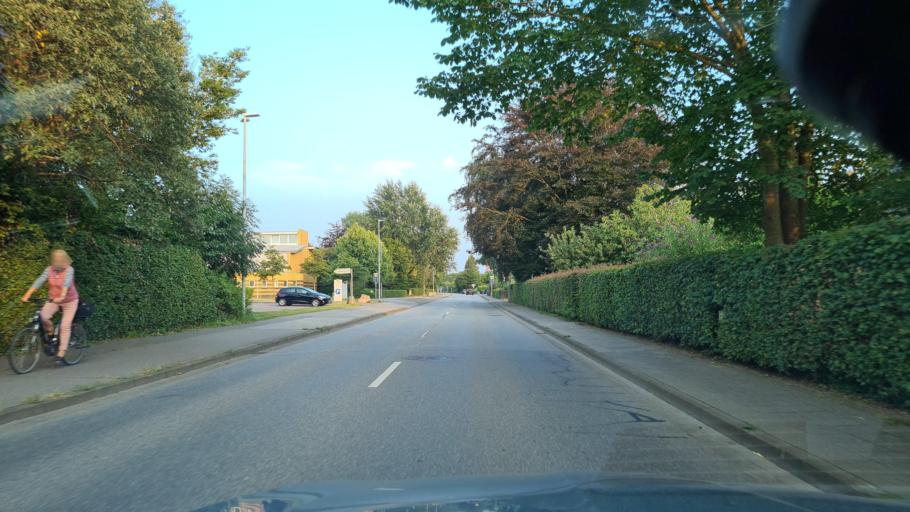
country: DE
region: Schleswig-Holstein
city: Husum
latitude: 54.4909
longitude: 9.0357
